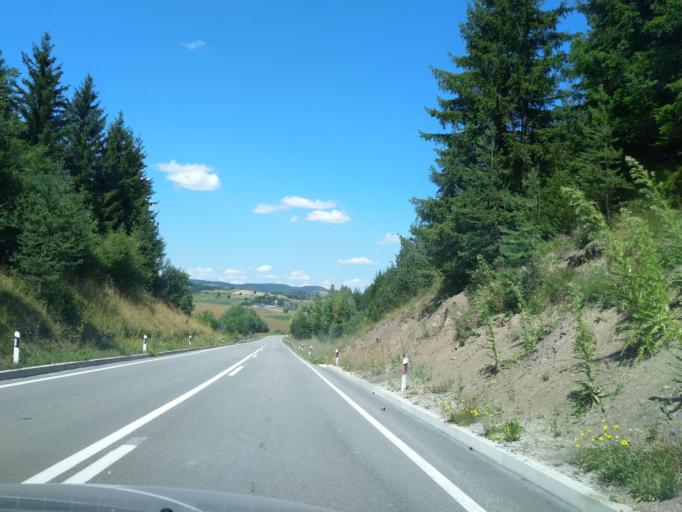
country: RS
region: Central Serbia
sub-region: Zlatiborski Okrug
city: Sjenica
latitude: 43.3189
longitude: 19.8934
